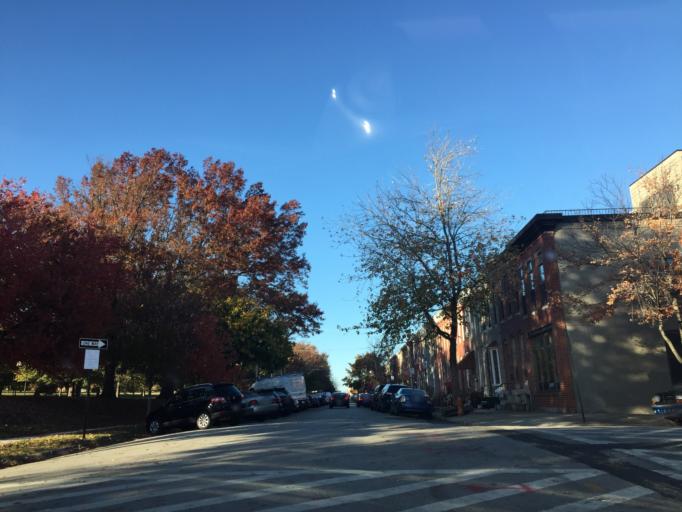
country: US
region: Maryland
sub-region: City of Baltimore
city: Baltimore
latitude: 39.2696
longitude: -76.6065
